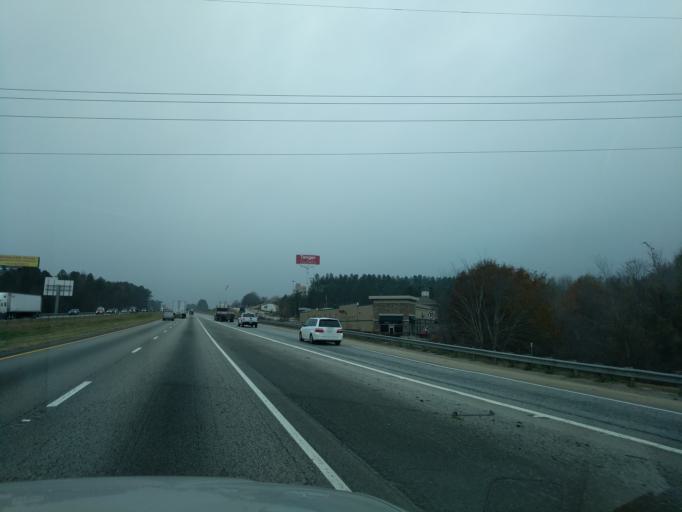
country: US
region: Georgia
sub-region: Jackson County
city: Commerce
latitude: 34.2539
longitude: -83.4634
